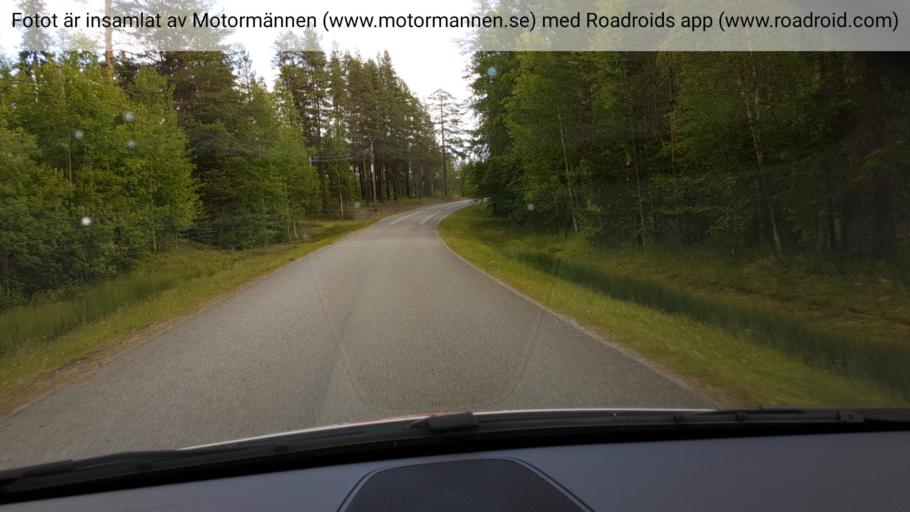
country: SE
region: Vaesterbotten
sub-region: Dorotea Kommun
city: Dorotea
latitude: 64.1064
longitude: 16.3621
